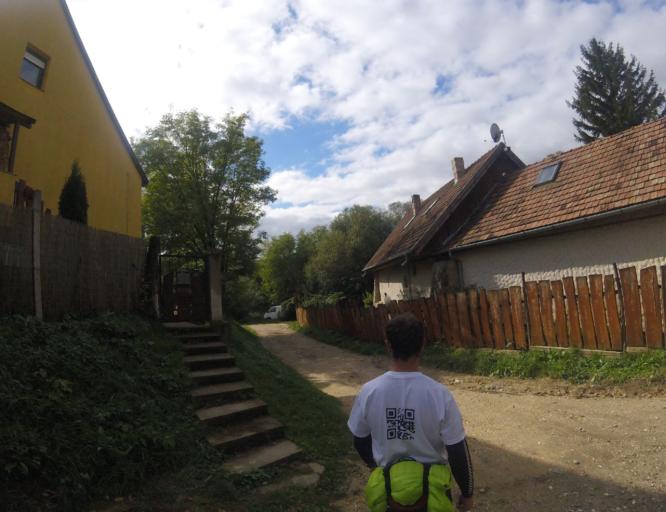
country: HU
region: Pest
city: Csobanka
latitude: 47.6478
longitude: 18.9606
